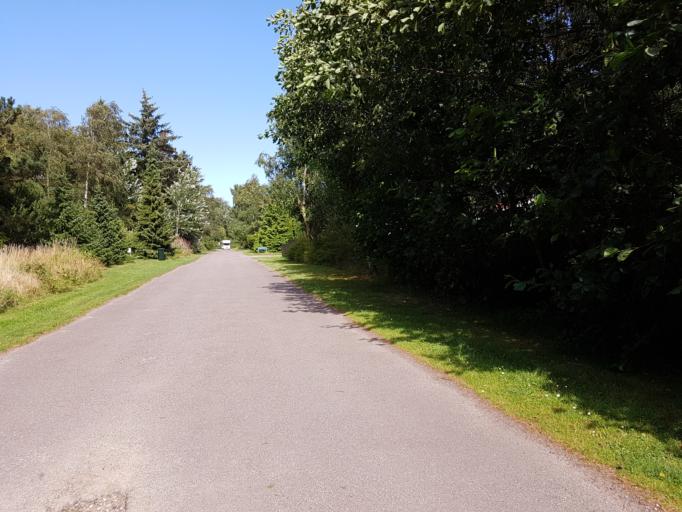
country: DK
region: Zealand
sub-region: Guldborgsund Kommune
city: Nykobing Falster
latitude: 54.6022
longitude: 11.9612
